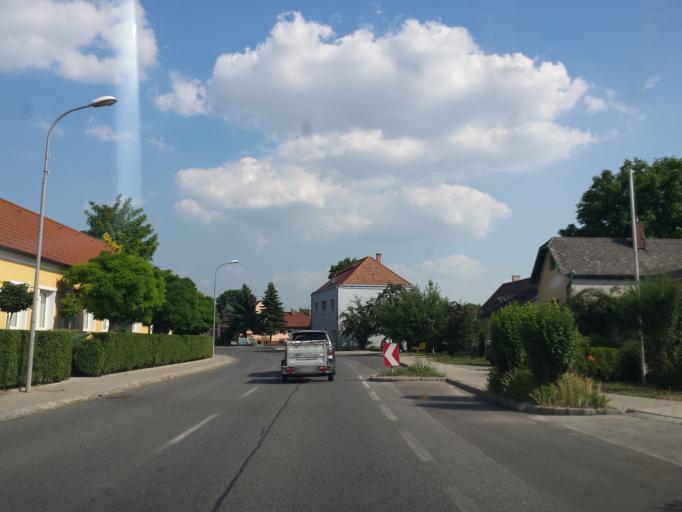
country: AT
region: Lower Austria
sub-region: Politischer Bezirk Ganserndorf
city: Untersiebenbrunn
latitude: 48.2549
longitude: 16.7459
